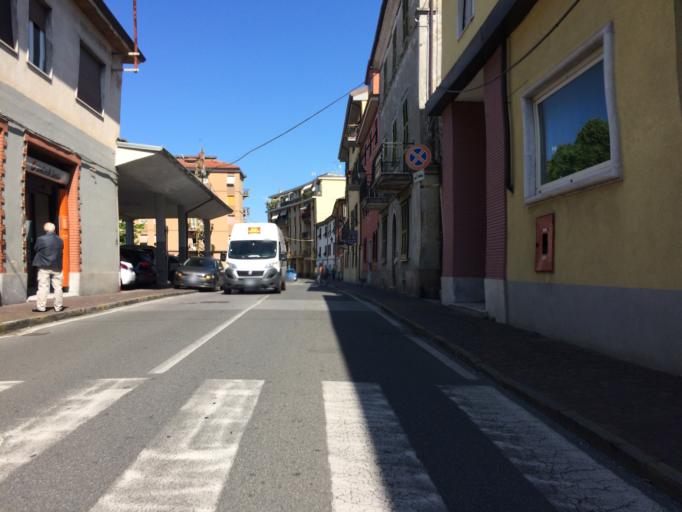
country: IT
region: Liguria
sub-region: Provincia di La Spezia
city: Sarzana
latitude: 44.1113
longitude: 9.9612
